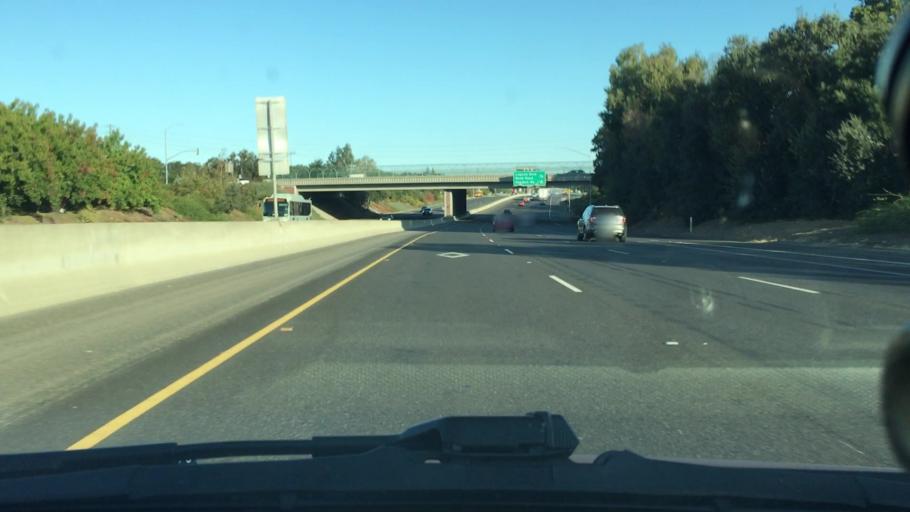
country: US
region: California
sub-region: Sacramento County
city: Elk Grove
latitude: 38.4078
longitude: -121.3879
